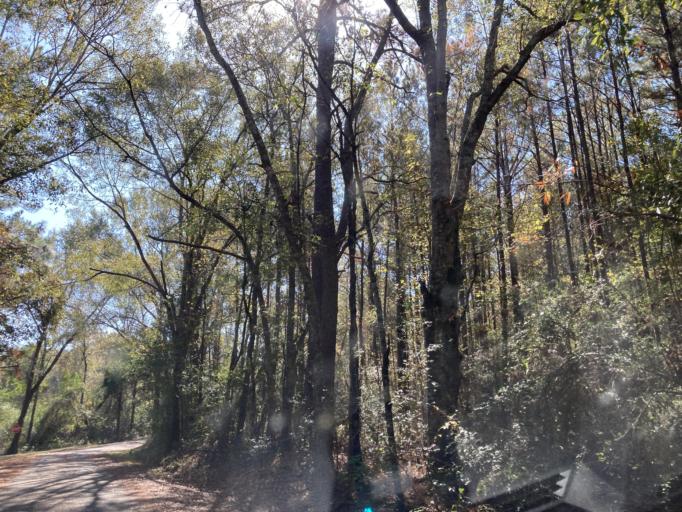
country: US
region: Mississippi
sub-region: Lamar County
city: Sumrall
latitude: 31.3320
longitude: -89.5139
